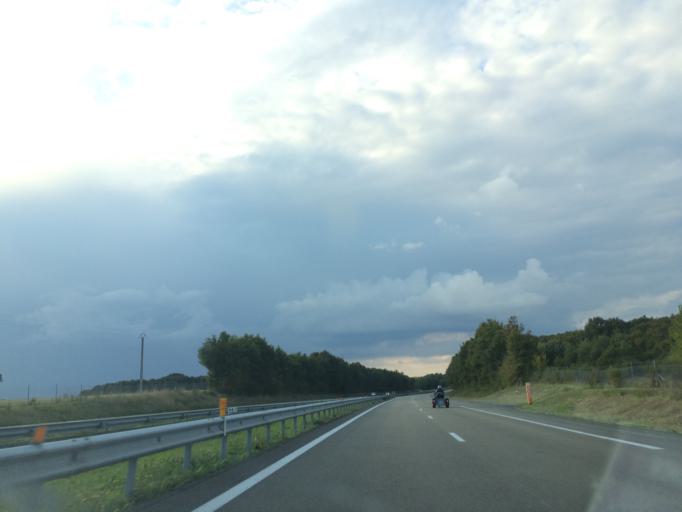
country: FR
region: Ile-de-France
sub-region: Departement de Seine-et-Marne
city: Egreville
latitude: 48.1364
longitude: 2.9222
